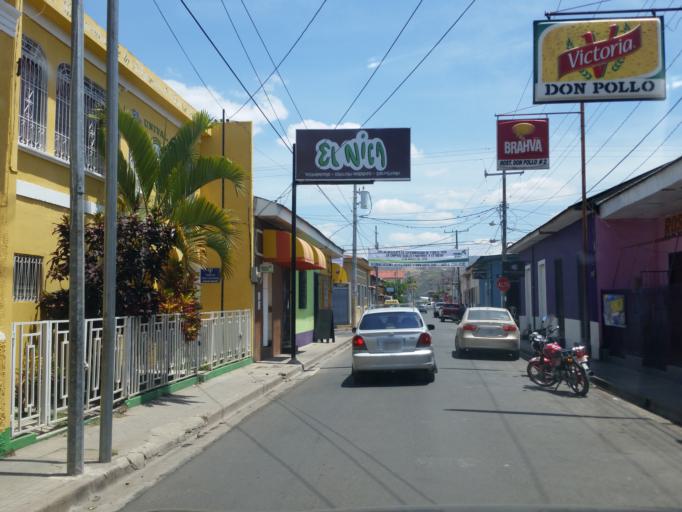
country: NI
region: Esteli
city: Esteli
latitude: 13.0943
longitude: -86.3554
